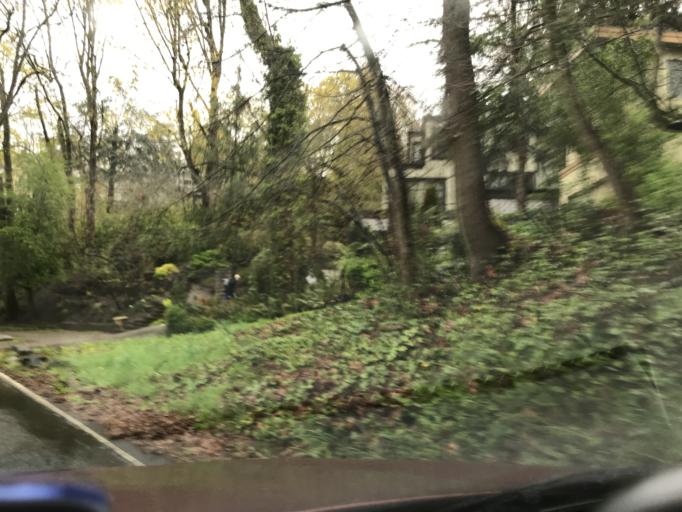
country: US
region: Washington
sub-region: King County
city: Seattle
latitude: 47.6244
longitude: -122.2907
